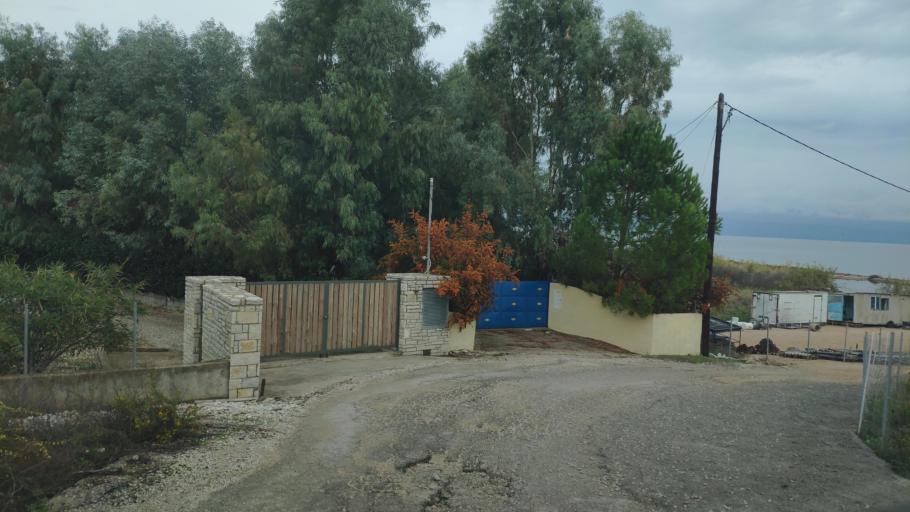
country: GR
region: West Greece
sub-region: Nomos Aitolias kai Akarnanias
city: Monastirakion
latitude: 38.9258
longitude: 21.0224
